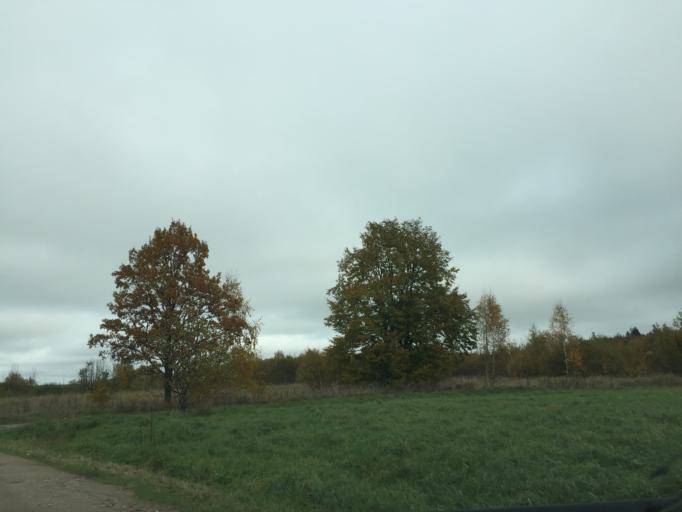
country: LV
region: Sigulda
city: Sigulda
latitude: 57.2409
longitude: 24.8315
